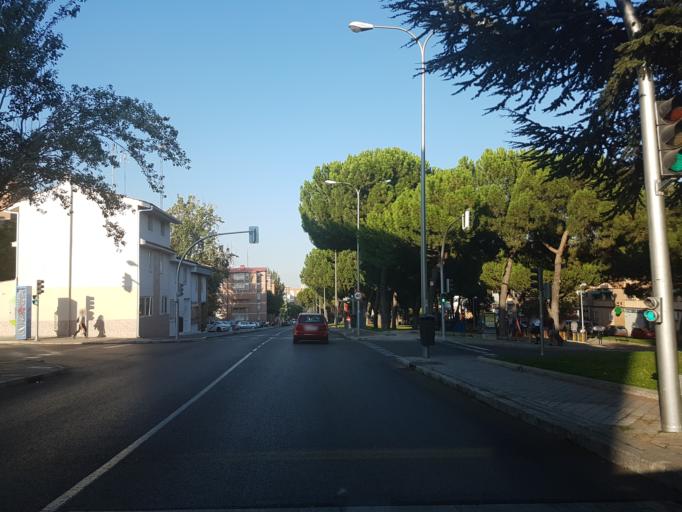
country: ES
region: Madrid
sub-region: Provincia de Madrid
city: Pinar de Chamartin
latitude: 40.4752
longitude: -3.6612
